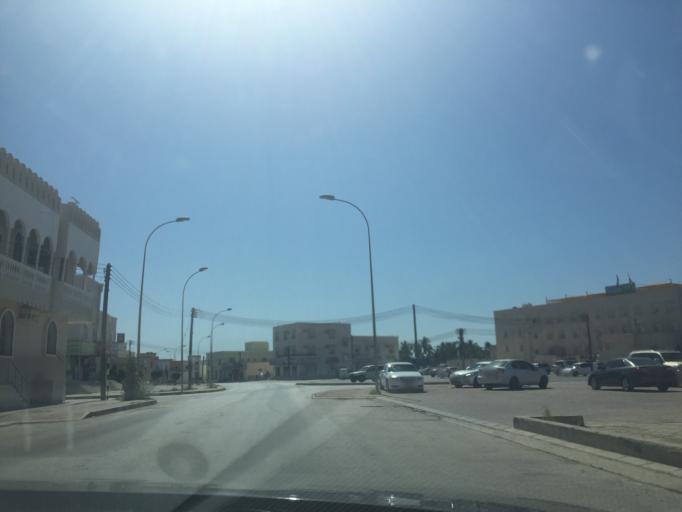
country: OM
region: Zufar
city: Salalah
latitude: 17.0227
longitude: 54.1564
